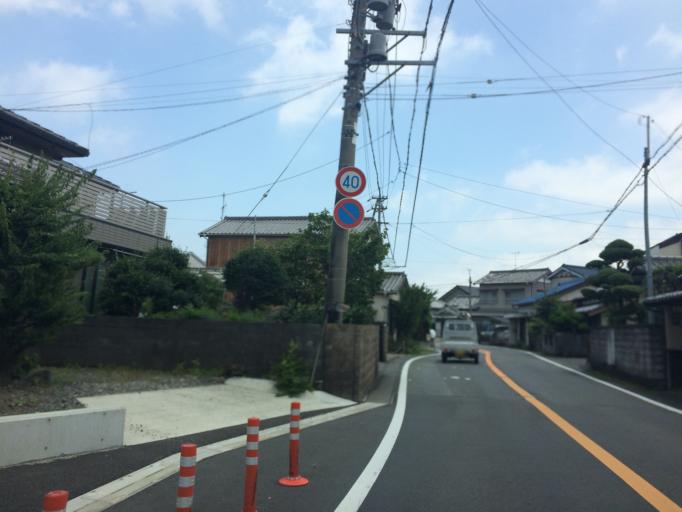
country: JP
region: Shizuoka
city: Fujieda
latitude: 34.8448
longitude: 138.2344
